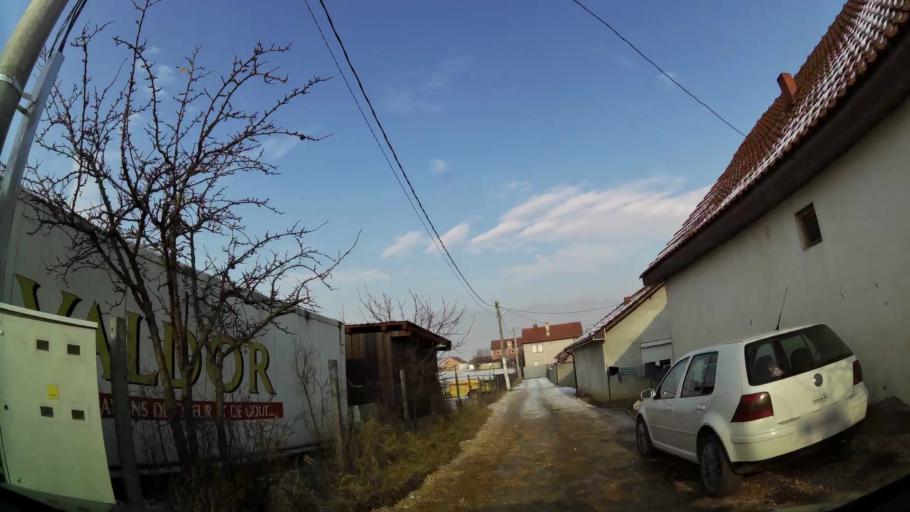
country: MK
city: Creshevo
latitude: 42.0219
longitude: 21.4976
